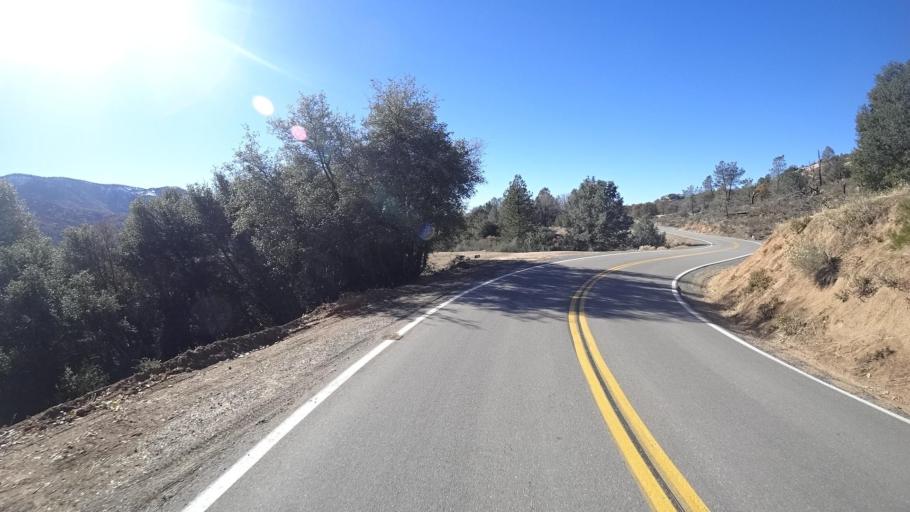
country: US
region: California
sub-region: Kern County
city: Alta Sierra
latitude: 35.7468
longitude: -118.5918
